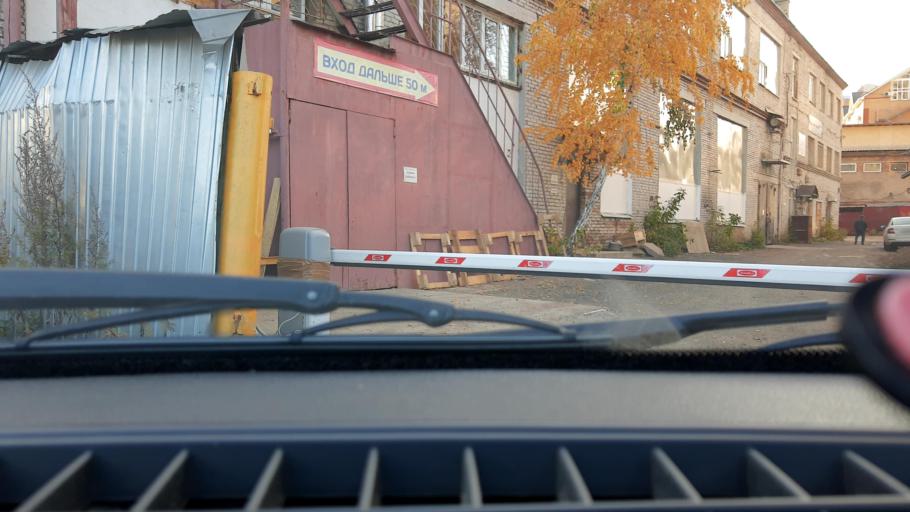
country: RU
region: Bashkortostan
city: Ufa
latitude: 54.7274
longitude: 55.9871
